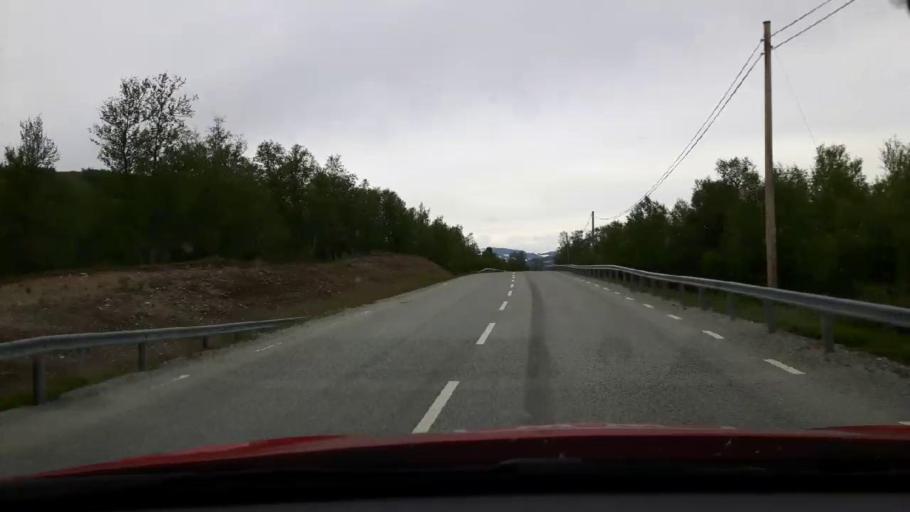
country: NO
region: Sor-Trondelag
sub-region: Tydal
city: Aas
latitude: 62.6976
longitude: 12.3975
